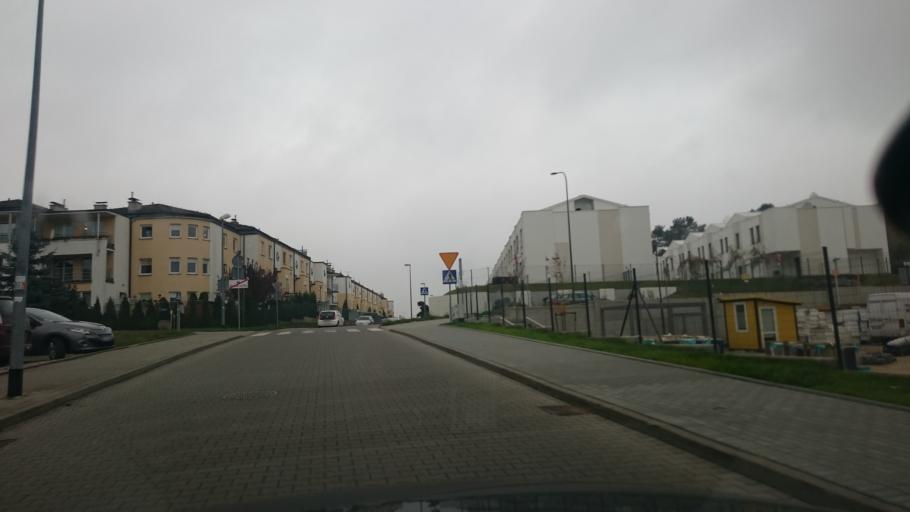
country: PL
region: Pomeranian Voivodeship
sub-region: Gdynia
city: Wielki Kack
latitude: 54.4696
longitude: 18.5186
